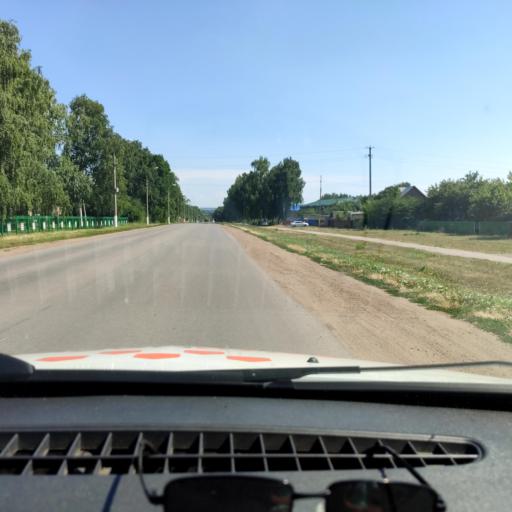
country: RU
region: Bashkortostan
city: Tolbazy
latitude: 54.0093
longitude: 55.8885
